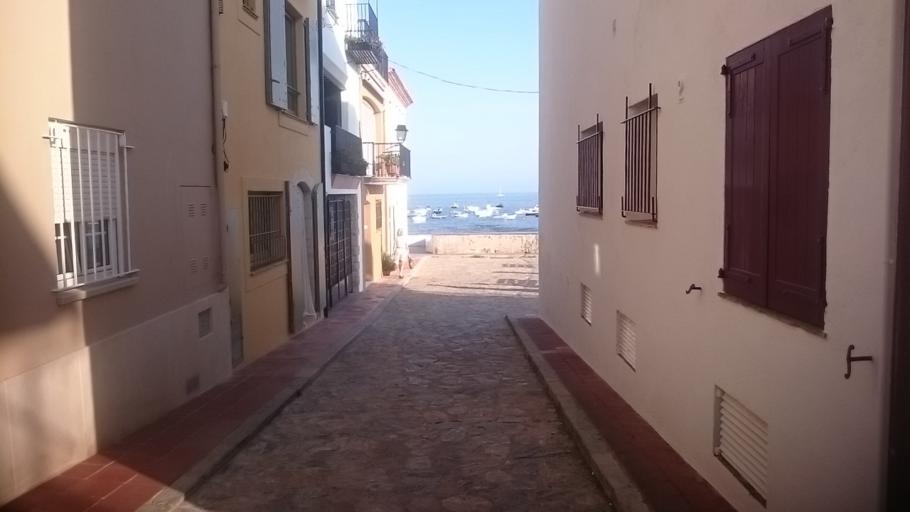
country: ES
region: Catalonia
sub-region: Provincia de Girona
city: Palafrugell
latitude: 41.8883
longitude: 3.1864
